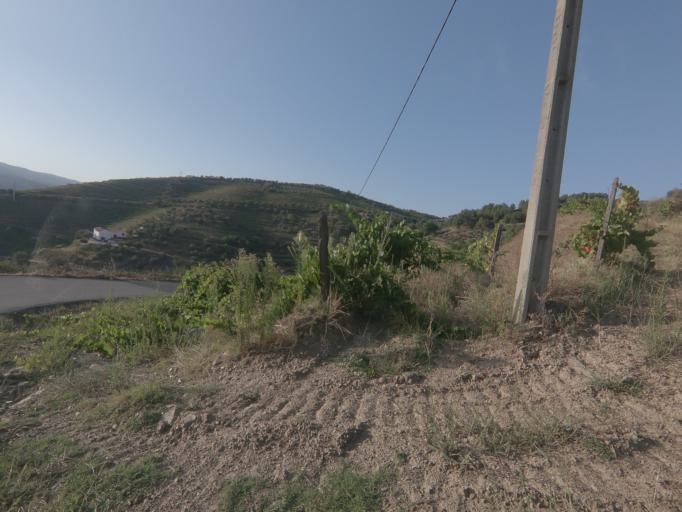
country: PT
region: Vila Real
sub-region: Sabrosa
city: Sabrosa
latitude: 41.2636
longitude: -7.5342
